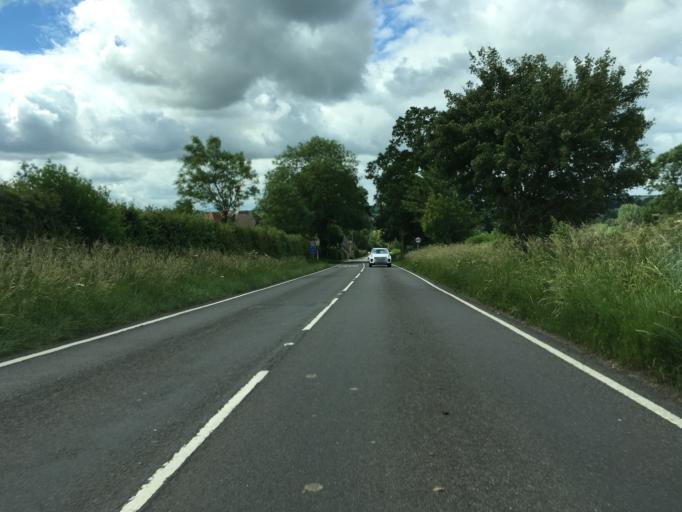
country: GB
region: England
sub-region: Oxfordshire
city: Shipton under Wychwood
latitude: 51.8667
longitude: -1.5891
